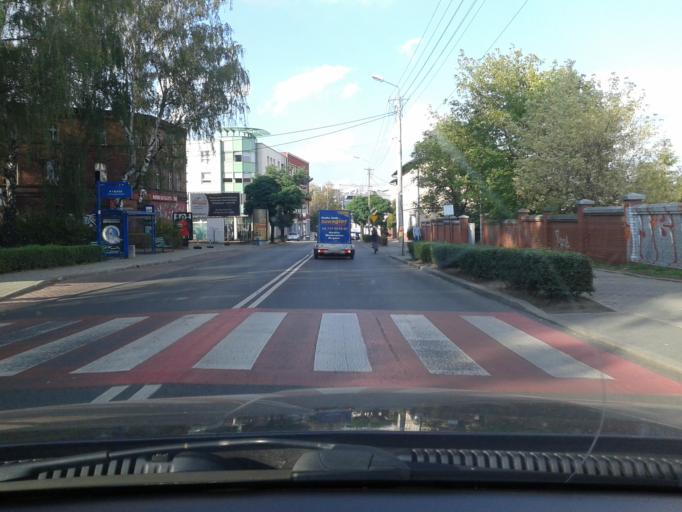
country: PL
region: Silesian Voivodeship
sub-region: Rybnik
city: Rybnik
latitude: 50.0939
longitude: 18.5357
